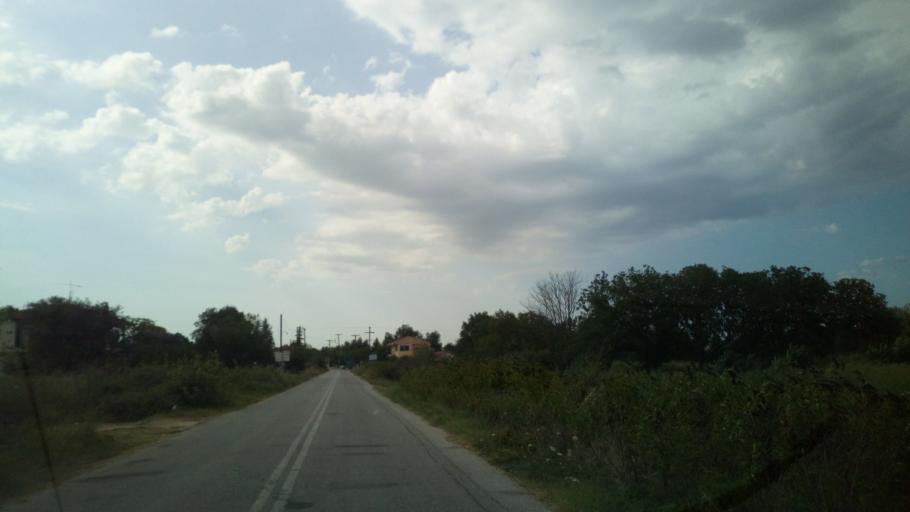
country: GR
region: Central Macedonia
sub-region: Nomos Thessalonikis
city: Gerakarou
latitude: 40.5660
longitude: 23.2900
